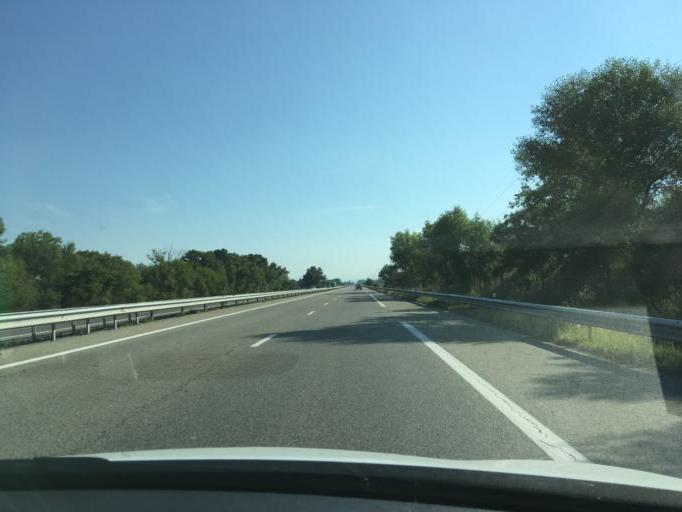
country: FR
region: Provence-Alpes-Cote d'Azur
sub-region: Departement des Alpes-de-Haute-Provence
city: Sainte-Tulle
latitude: 43.7445
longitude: 5.7608
